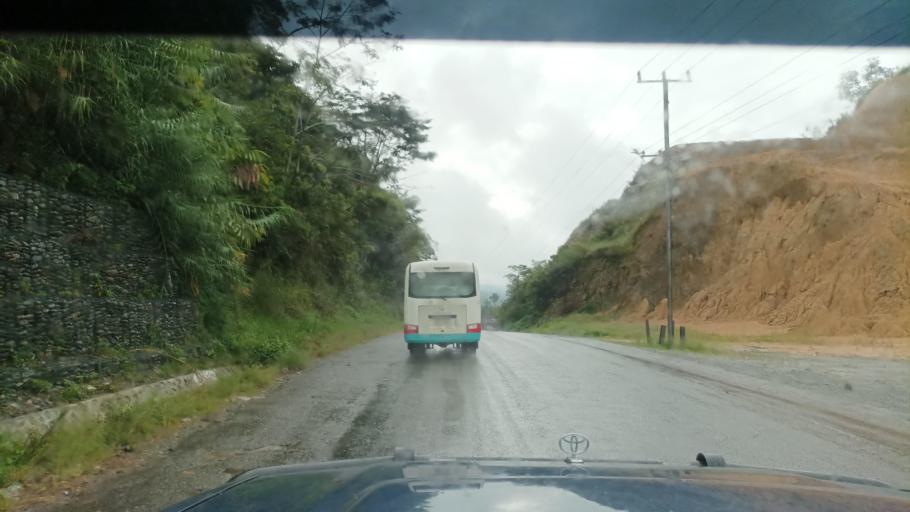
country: PG
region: Western Highlands
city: Rauna
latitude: -5.8277
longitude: 144.3723
